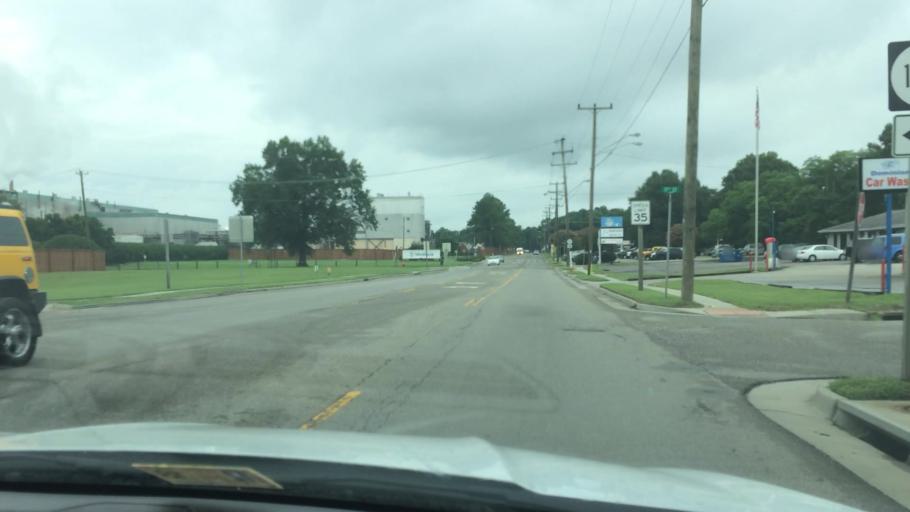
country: US
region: Virginia
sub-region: King William County
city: West Point
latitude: 37.5390
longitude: -76.8004
